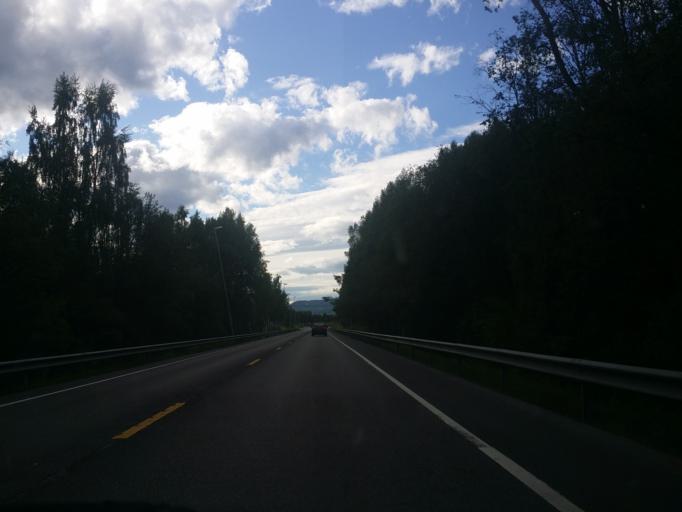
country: NO
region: Hedmark
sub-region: Hamar
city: Hamar
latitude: 60.8092
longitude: 11.1057
